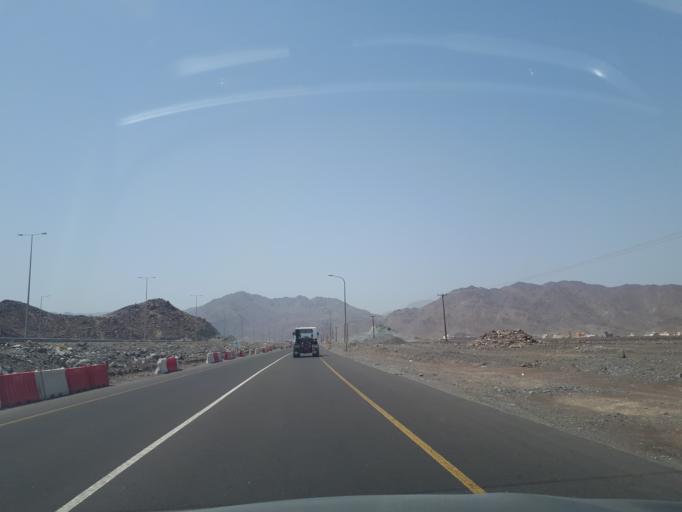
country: OM
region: Muhafazat ad Dakhiliyah
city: Sufalat Sama'il
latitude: 23.2783
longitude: 58.1068
